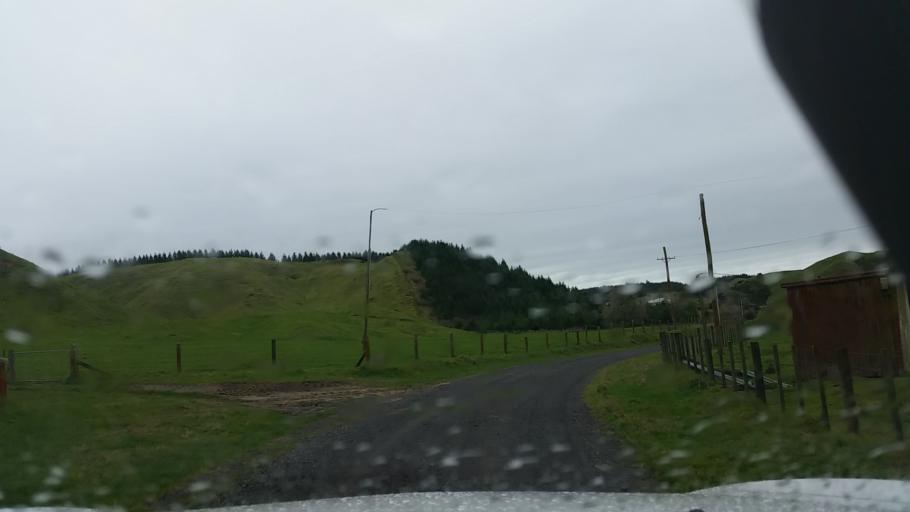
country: NZ
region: Bay of Plenty
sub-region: Western Bay of Plenty District
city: Maketu
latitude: -37.9782
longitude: 176.4051
